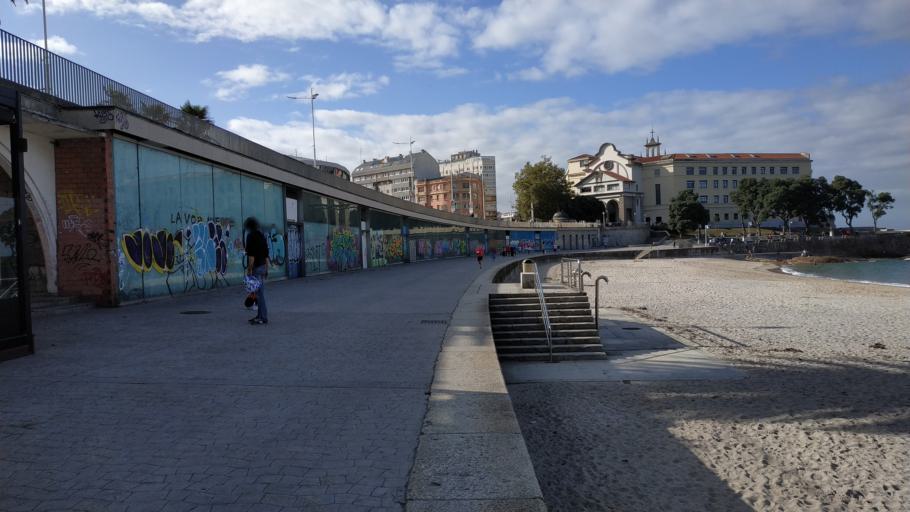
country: ES
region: Galicia
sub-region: Provincia da Coruna
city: A Coruna
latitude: 43.3688
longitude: -8.4137
